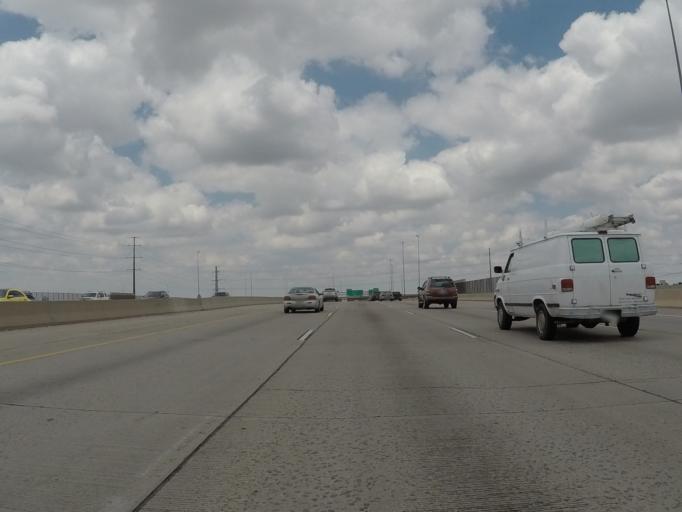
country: US
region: Colorado
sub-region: Adams County
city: Aurora
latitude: 39.7635
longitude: -104.8276
